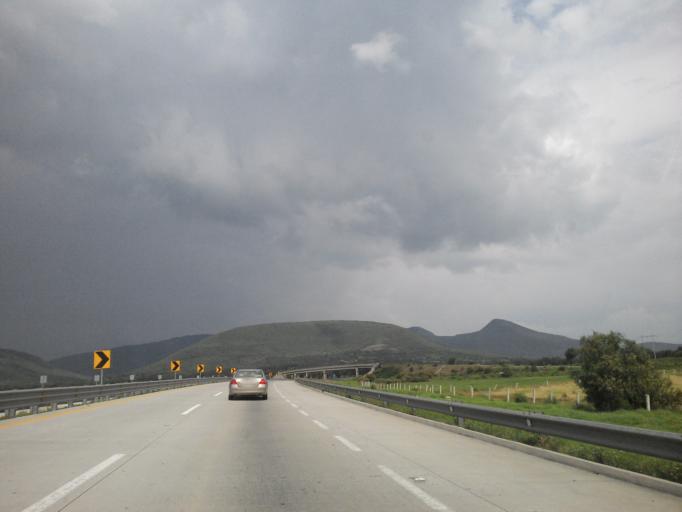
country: MX
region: Hidalgo
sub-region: Atitalaquia
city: Tezoquipa
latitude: 20.0612
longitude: -99.1994
